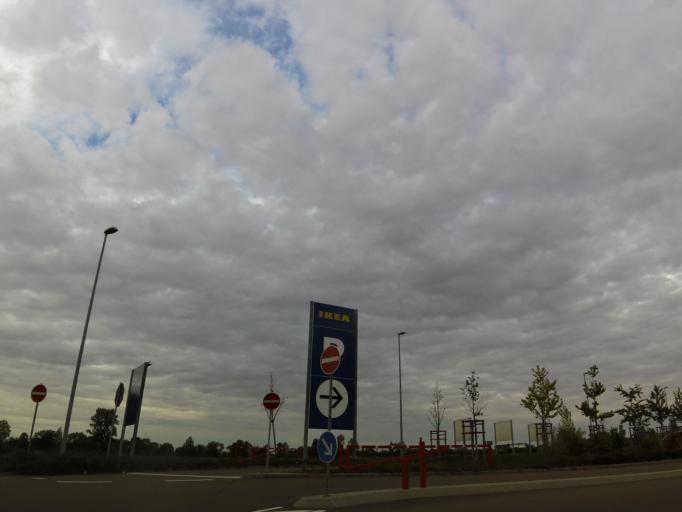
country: DE
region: Saxony-Anhalt
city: Gunthersdorf
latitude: 51.3496
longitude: 12.1805
